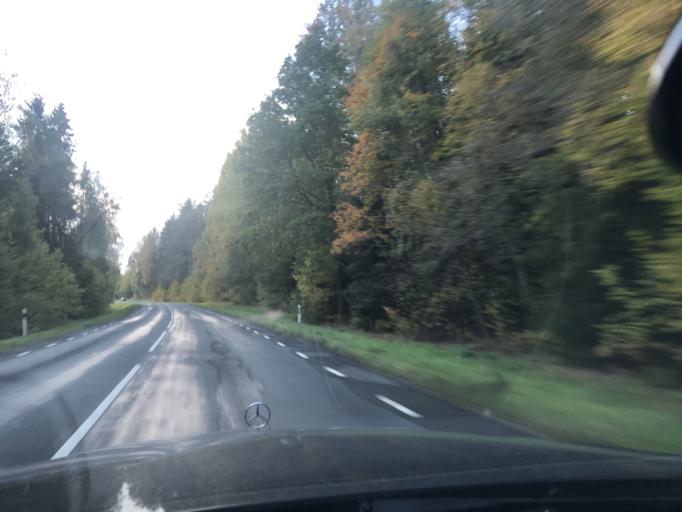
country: EE
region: Vorumaa
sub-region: Antsla vald
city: Vana-Antsla
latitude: 57.8800
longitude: 26.5775
